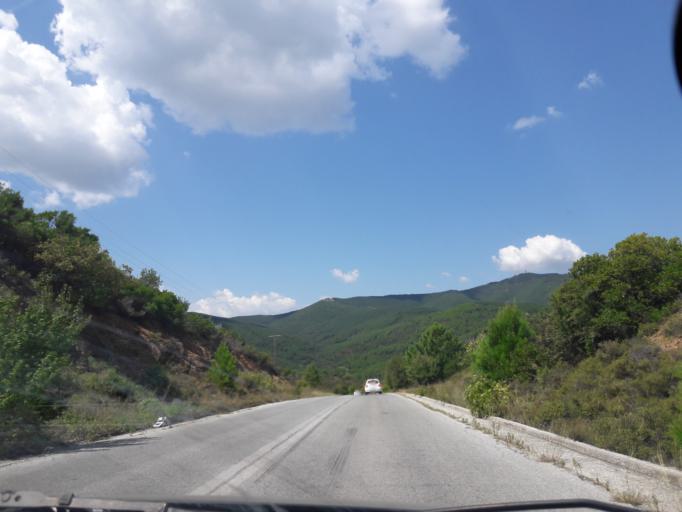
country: GR
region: Central Macedonia
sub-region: Nomos Chalkidikis
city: Polygyros
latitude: 40.3690
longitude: 23.5074
